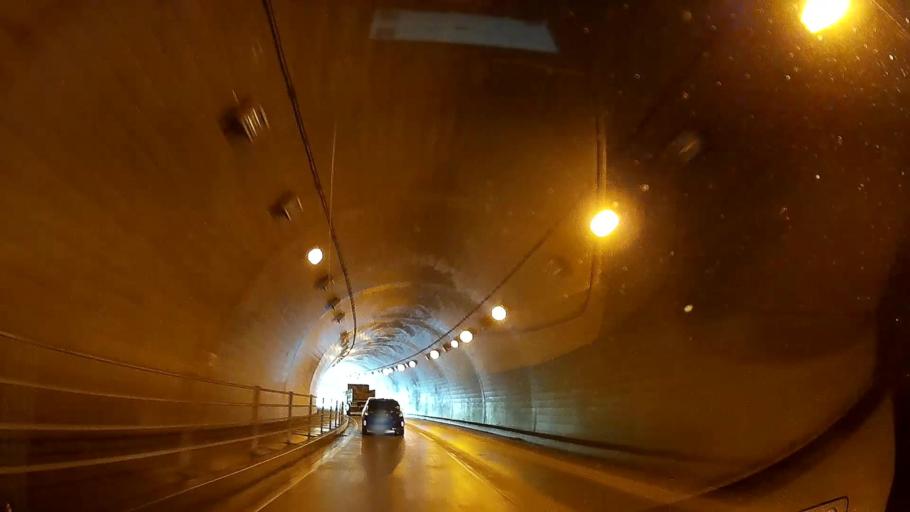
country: JP
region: Kumamoto
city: Aso
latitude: 33.1218
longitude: 131.0174
